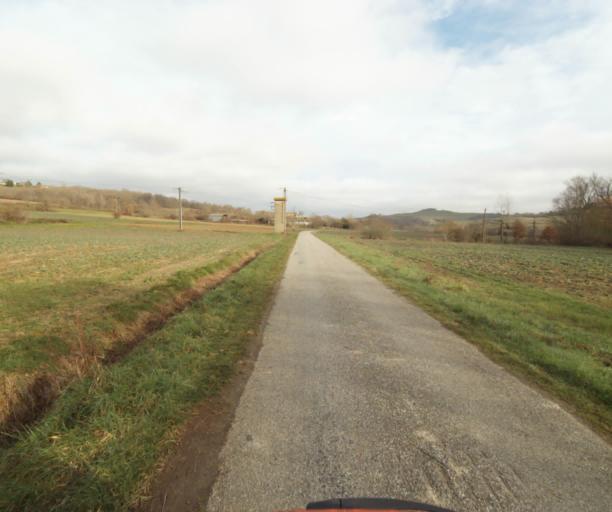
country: FR
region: Midi-Pyrenees
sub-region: Departement de l'Ariege
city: Saverdun
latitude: 43.1838
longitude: 1.5172
